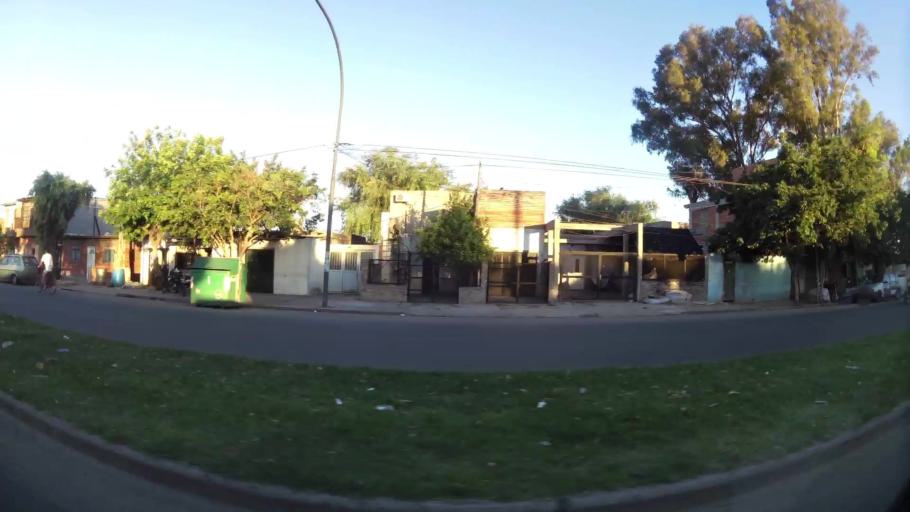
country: AR
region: Santa Fe
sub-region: Departamento de Rosario
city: Rosario
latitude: -32.9646
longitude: -60.6856
